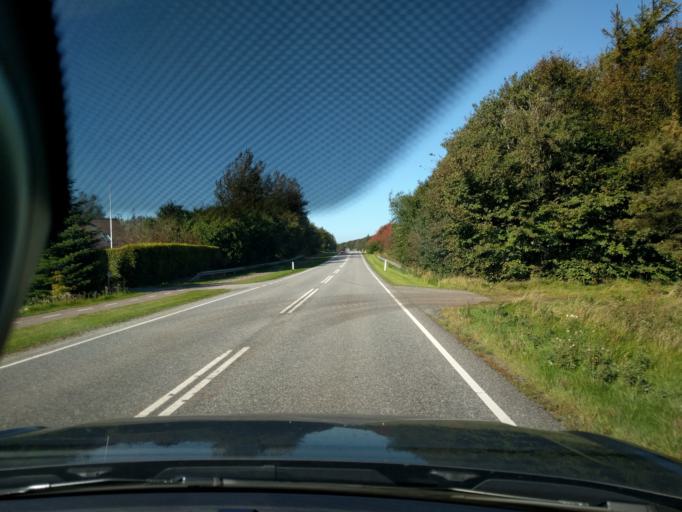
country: DK
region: North Denmark
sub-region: Mariagerfjord Kommune
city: Hobro
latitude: 56.6959
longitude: 9.6485
